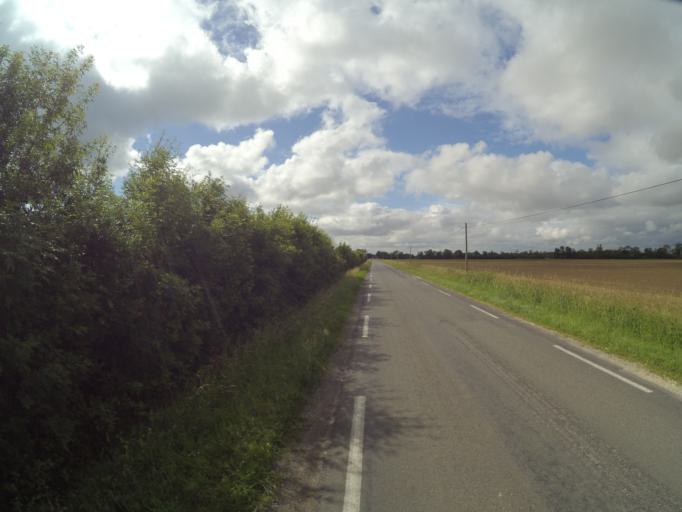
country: FR
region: Aquitaine
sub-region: Departement de la Gironde
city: Saint-Louis-de-Montferrand
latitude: 44.9766
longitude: -0.5602
